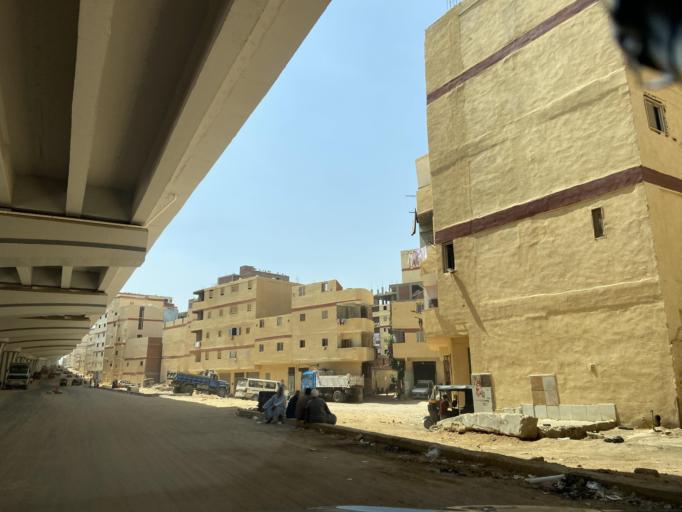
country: EG
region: Muhafazat al Qahirah
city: Cairo
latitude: 30.0692
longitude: 31.3860
